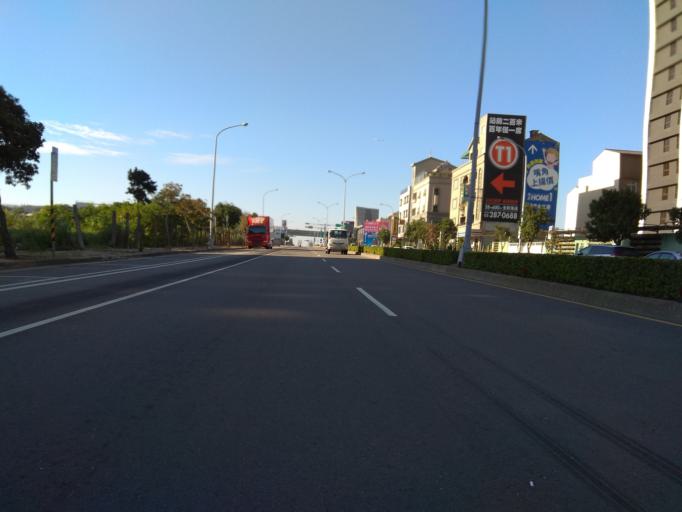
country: TW
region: Taiwan
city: Taoyuan City
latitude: 25.0150
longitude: 121.2209
